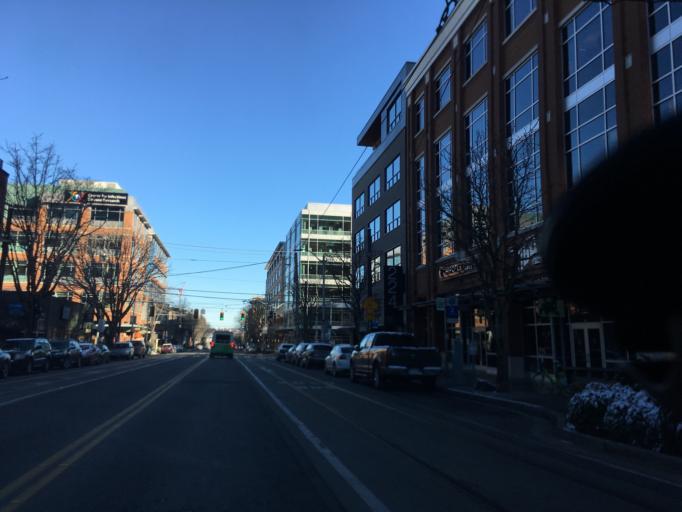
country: US
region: Washington
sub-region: King County
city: Seattle
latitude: 47.6200
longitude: -122.3385
